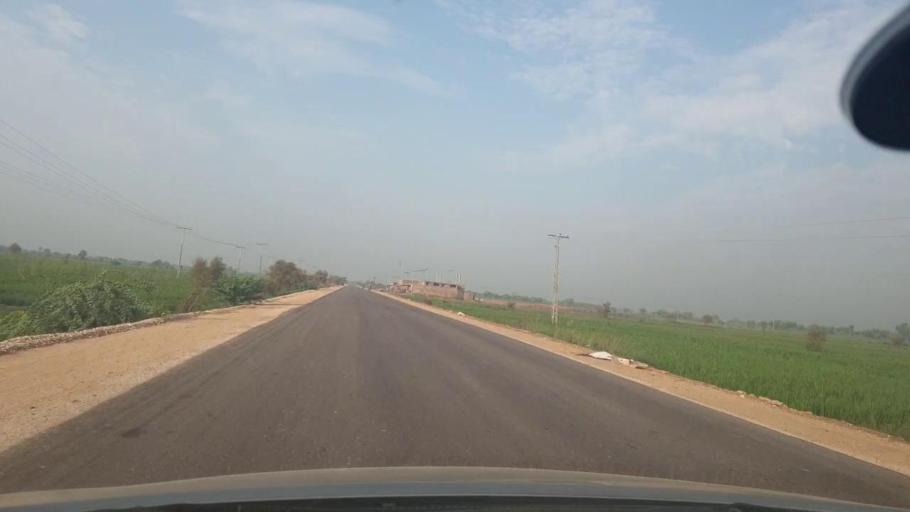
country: PK
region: Sindh
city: Jacobabad
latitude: 28.2555
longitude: 68.4094
